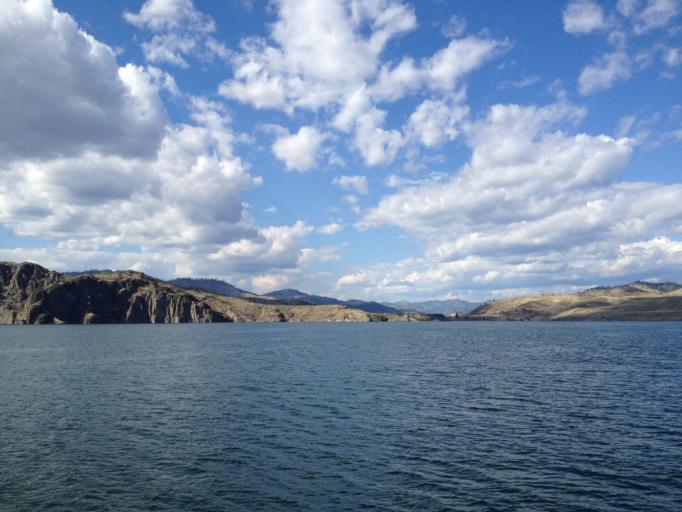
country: US
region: Washington
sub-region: Okanogan County
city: Coulee Dam
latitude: 47.9328
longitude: -118.6916
